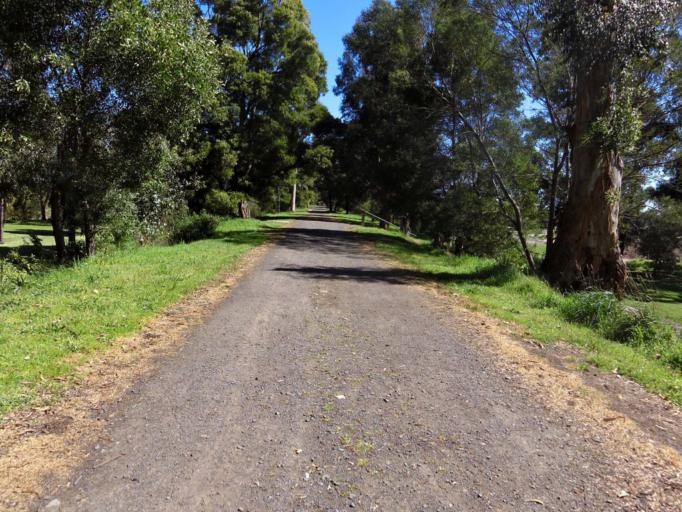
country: AU
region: Victoria
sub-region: Latrobe
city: Moe
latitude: -38.1762
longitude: 146.2714
